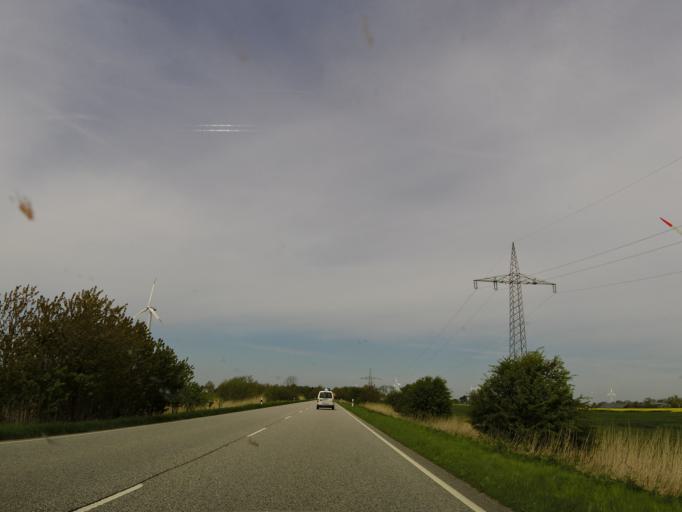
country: DE
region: Schleswig-Holstein
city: Hemme
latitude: 54.2705
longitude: 9.0184
